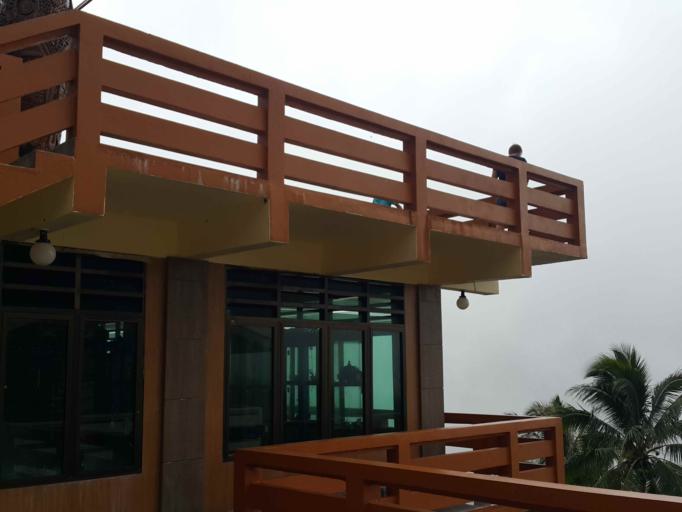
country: TH
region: Chiang Mai
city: Chiang Mai
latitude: 18.8045
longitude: 98.9217
